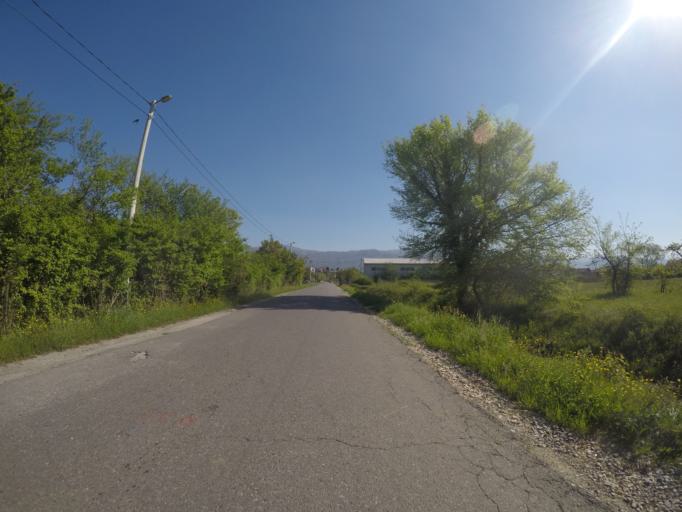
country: ME
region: Danilovgrad
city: Danilovgrad
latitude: 42.5437
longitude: 19.0969
